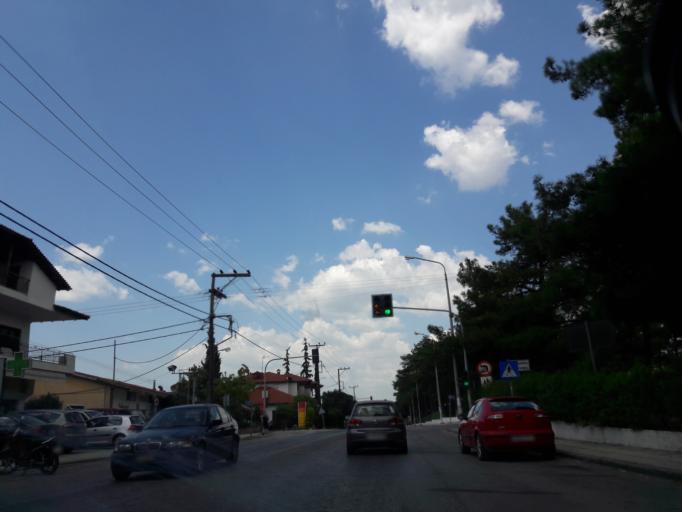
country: GR
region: Central Macedonia
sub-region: Nomos Thessalonikis
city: Thermi
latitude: 40.5243
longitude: 23.0503
